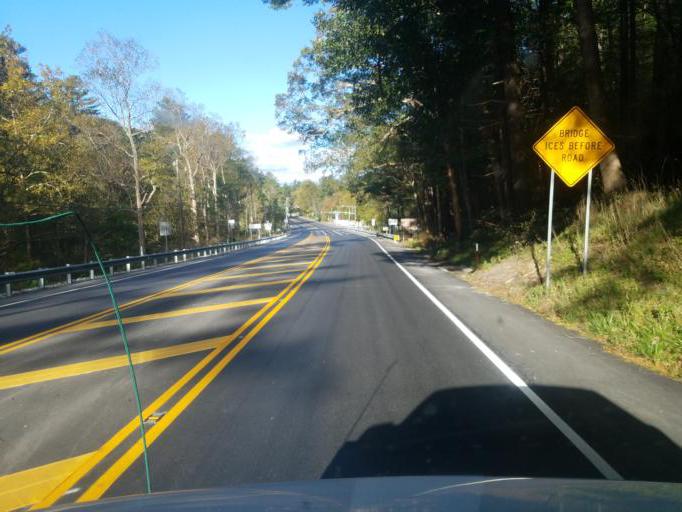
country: US
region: Pennsylvania
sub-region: Franklin County
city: Fayetteville
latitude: 39.9058
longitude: -77.4757
